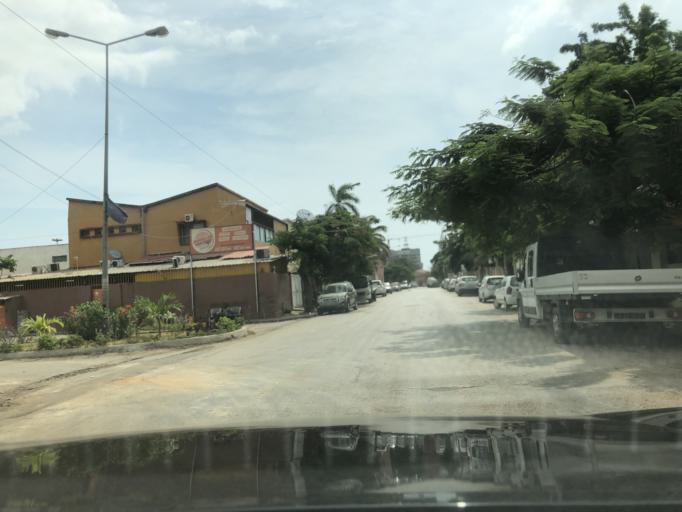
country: AO
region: Luanda
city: Luanda
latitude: -8.8299
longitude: 13.2500
